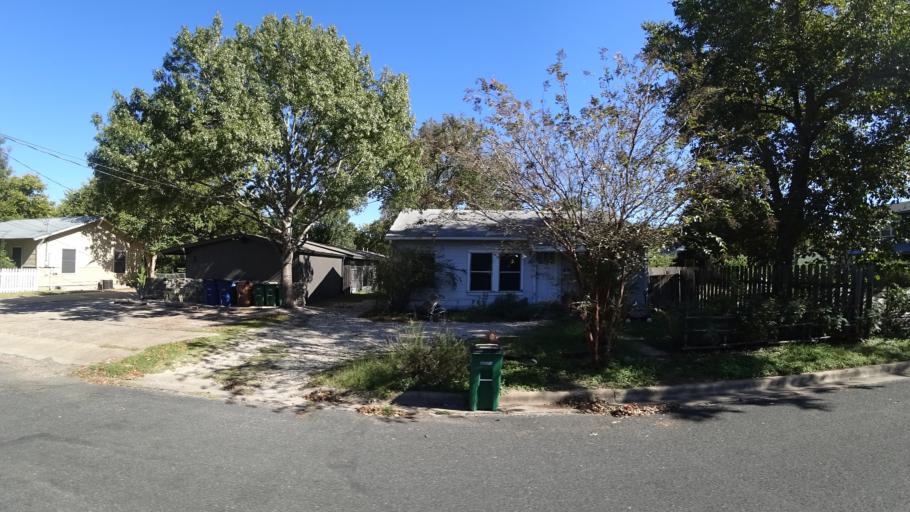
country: US
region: Texas
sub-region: Travis County
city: Austin
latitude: 30.3284
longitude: -97.7363
